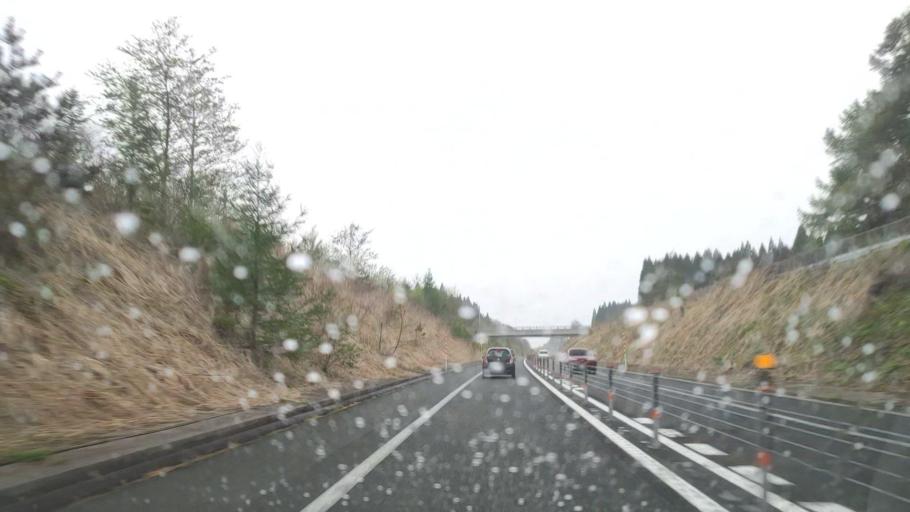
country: JP
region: Akita
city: Noshiromachi
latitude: 40.2013
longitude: 140.1485
